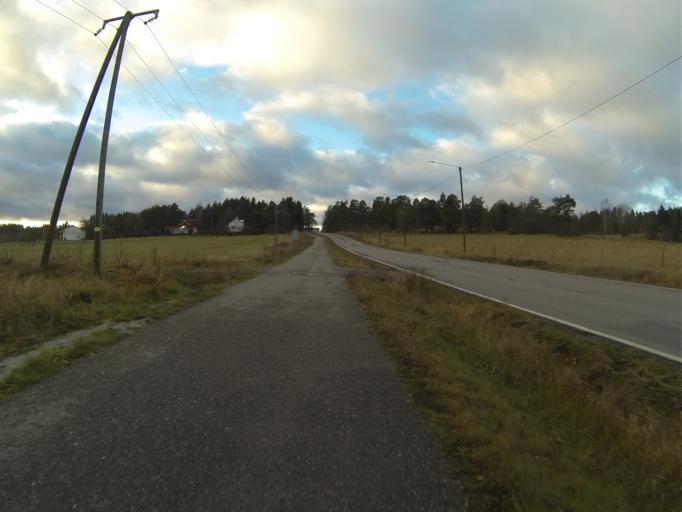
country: FI
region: Varsinais-Suomi
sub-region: Salo
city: Halikko
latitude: 60.3974
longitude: 23.0640
